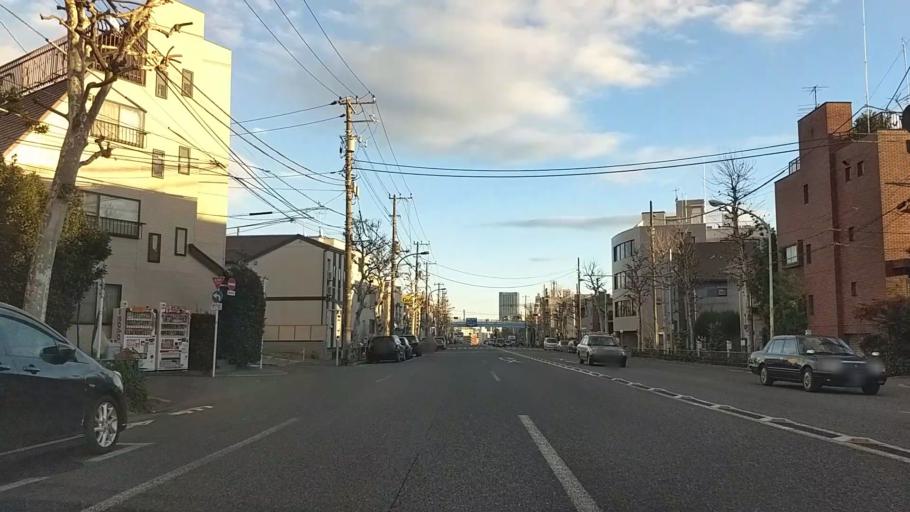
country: JP
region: Tokyo
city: Tokyo
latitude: 35.7219
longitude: 139.6851
